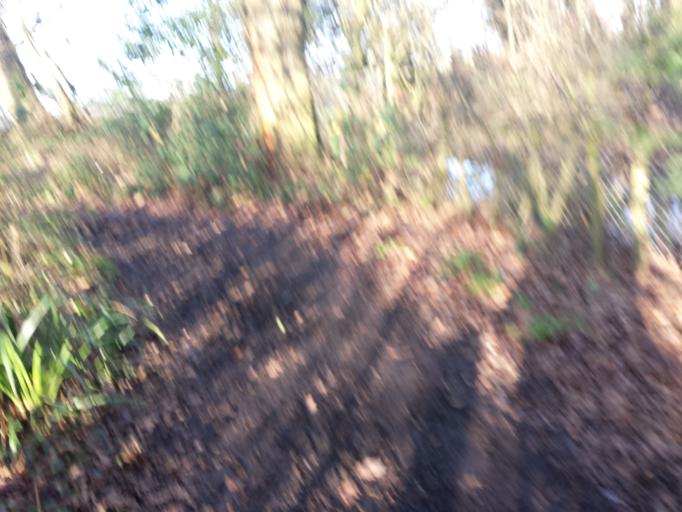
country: GB
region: England
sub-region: Essex
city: Alresford
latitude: 51.8580
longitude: 0.9907
